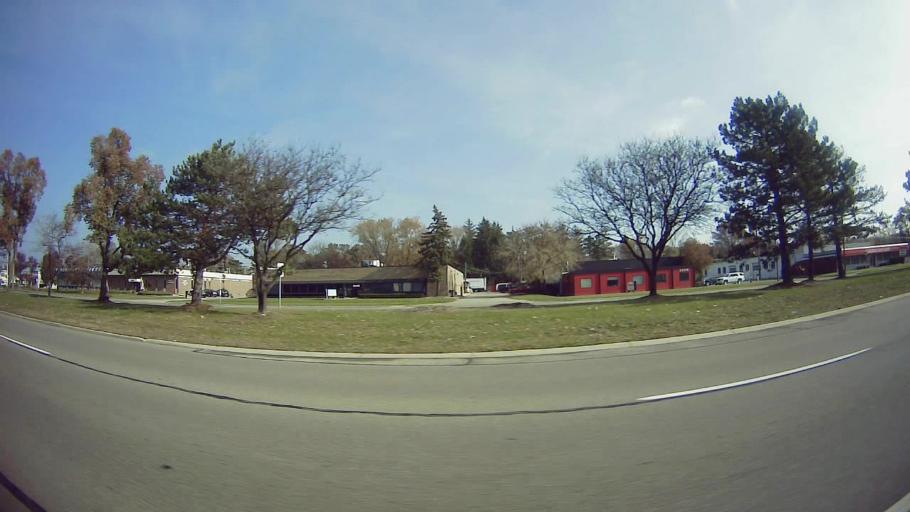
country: US
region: Michigan
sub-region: Oakland County
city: Southfield
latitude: 42.4548
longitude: -83.2786
